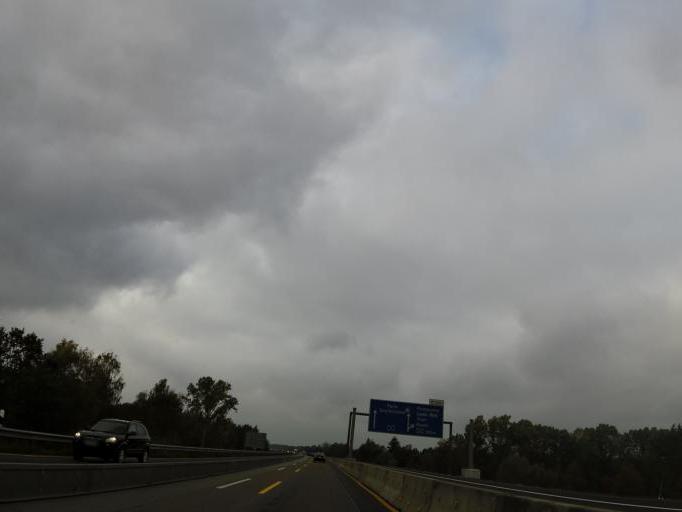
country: DE
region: Rheinland-Pfalz
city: Landstuhl
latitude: 49.4204
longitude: 7.5457
